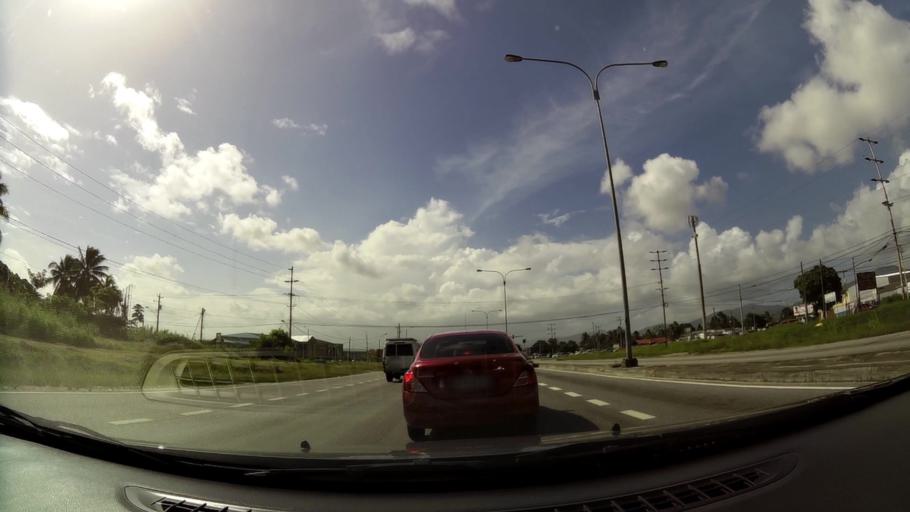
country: TT
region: Borough of Arima
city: Arima
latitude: 10.6092
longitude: -61.2897
